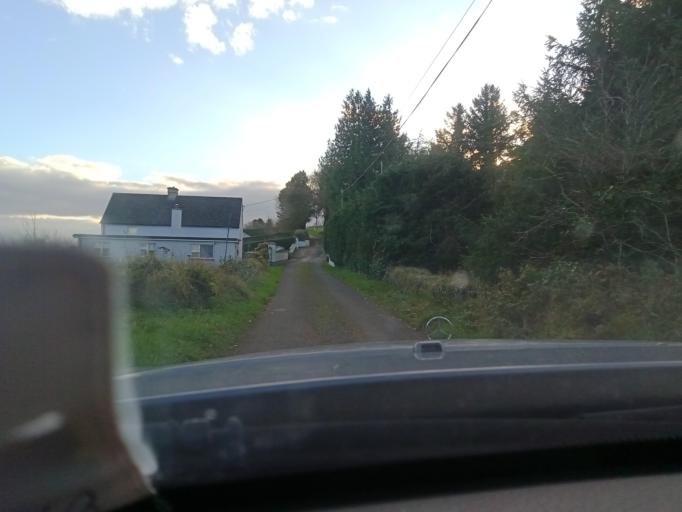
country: IE
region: Leinster
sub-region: Kilkenny
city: Graiguenamanagh
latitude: 52.5011
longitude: -6.9437
